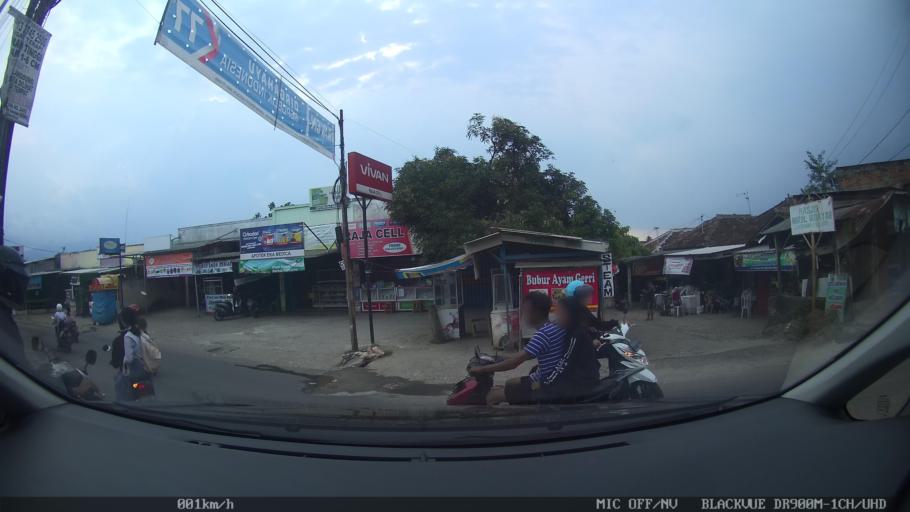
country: ID
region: Lampung
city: Kedaton
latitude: -5.3542
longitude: 105.2387
